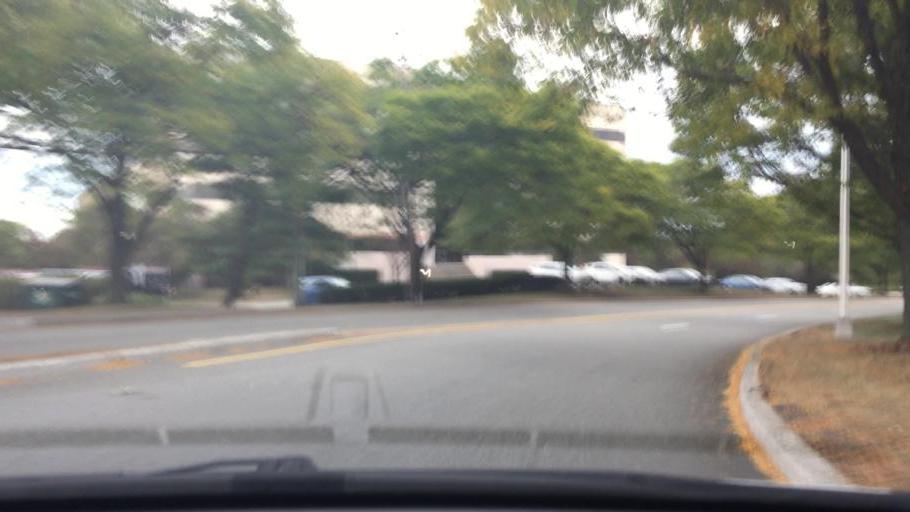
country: US
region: New Jersey
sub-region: Bergen County
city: Paramus
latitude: 40.9536
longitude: -74.0725
